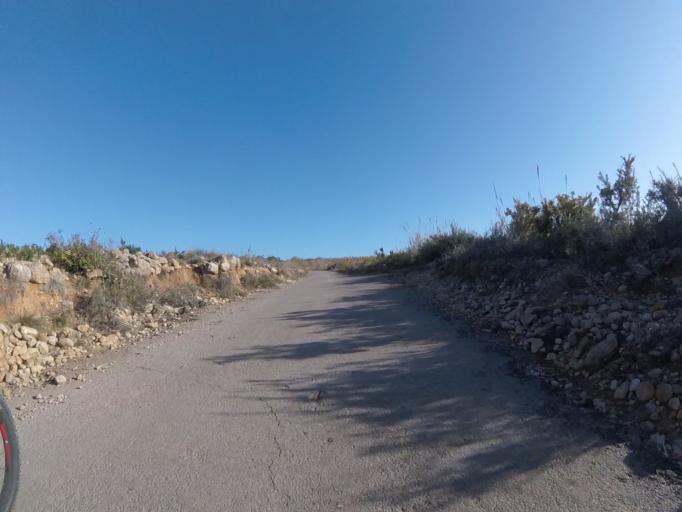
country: ES
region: Valencia
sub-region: Provincia de Castello
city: Alcala de Xivert
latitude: 40.2661
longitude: 0.2056
